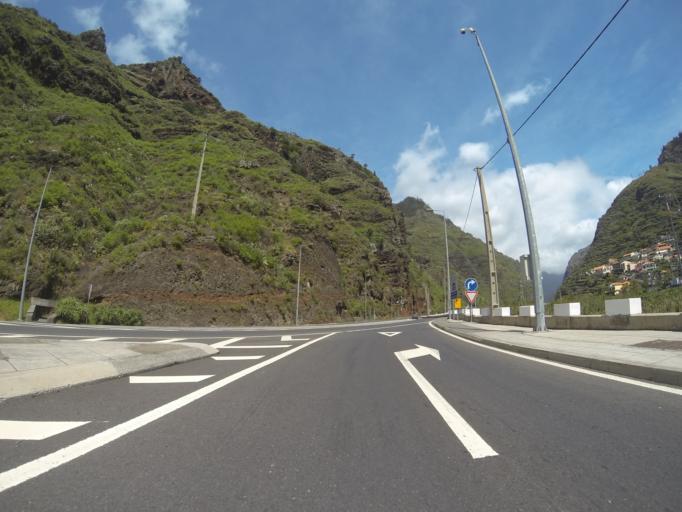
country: PT
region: Madeira
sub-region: Ribeira Brava
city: Campanario
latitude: 32.6857
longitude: -17.0513
